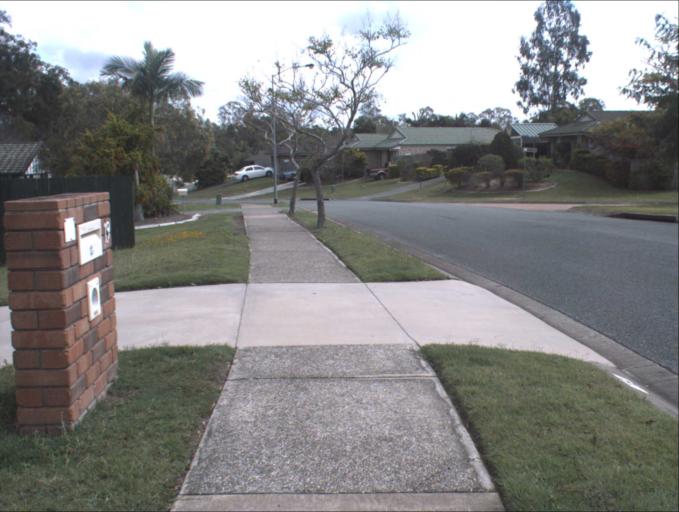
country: AU
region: Queensland
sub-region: Logan
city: Park Ridge South
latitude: -27.6829
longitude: 153.0406
